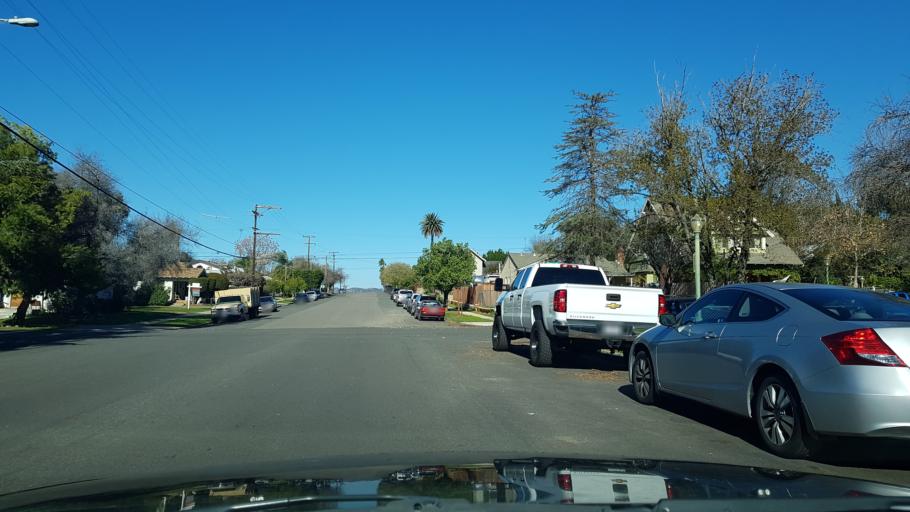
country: US
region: California
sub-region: San Diego County
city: Escondido
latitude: 33.1126
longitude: -117.0769
